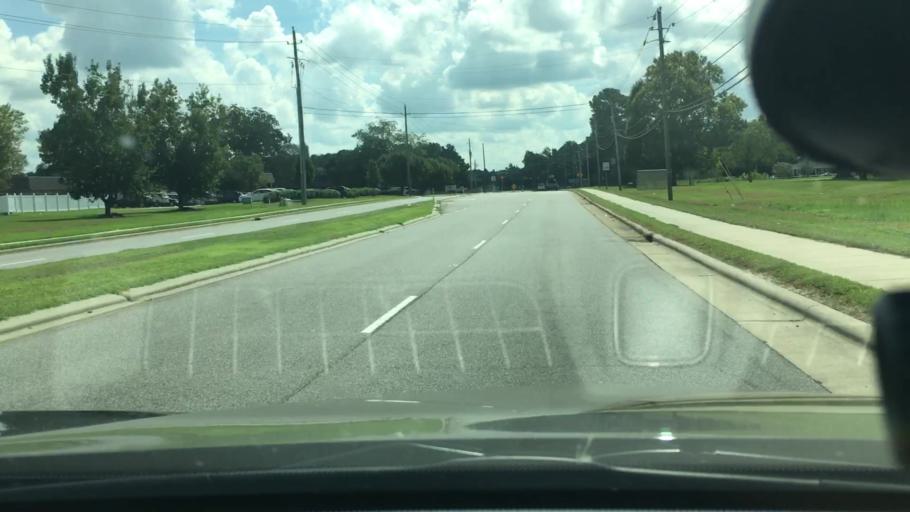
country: US
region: North Carolina
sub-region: Pitt County
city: Greenville
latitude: 35.6182
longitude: -77.4128
